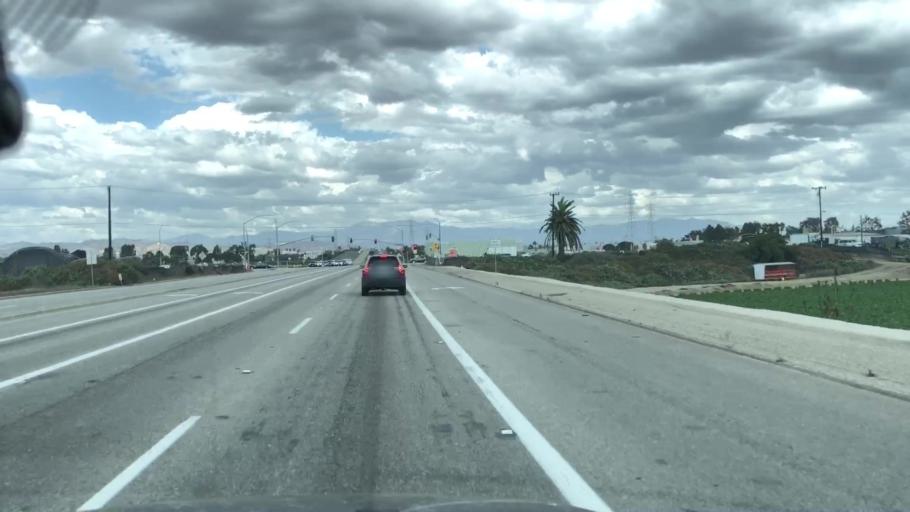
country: US
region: California
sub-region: Ventura County
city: El Rio
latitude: 34.2424
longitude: -119.2157
